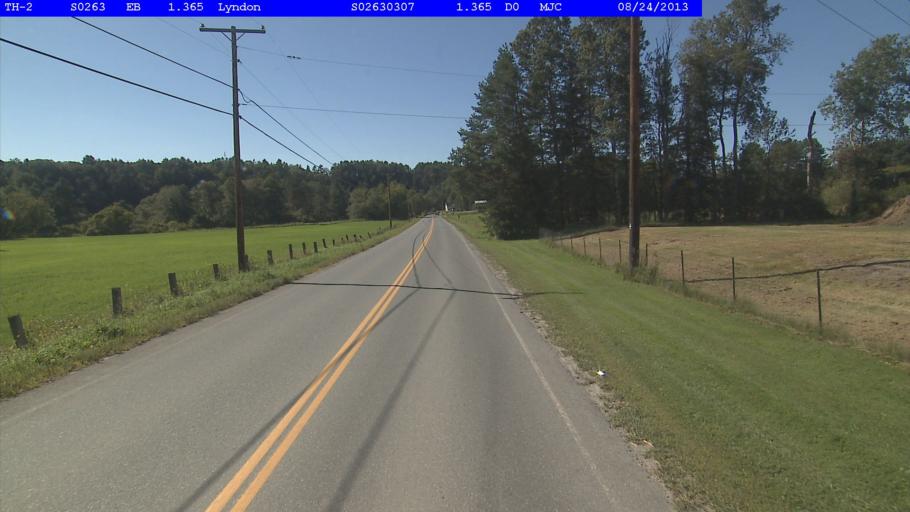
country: US
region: Vermont
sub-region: Caledonia County
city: Lyndon
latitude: 44.5058
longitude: -71.9876
